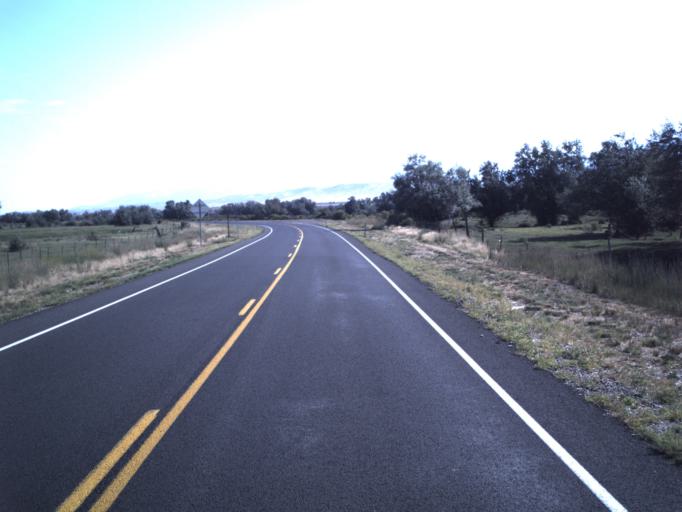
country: US
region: Utah
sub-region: Sevier County
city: Salina
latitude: 39.0097
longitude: -111.8567
